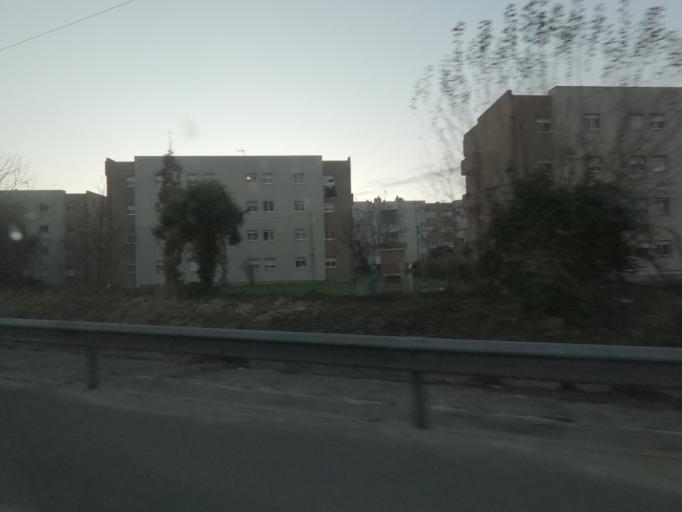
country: PT
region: Porto
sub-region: Porto
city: Porto
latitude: 41.1764
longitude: -8.6226
